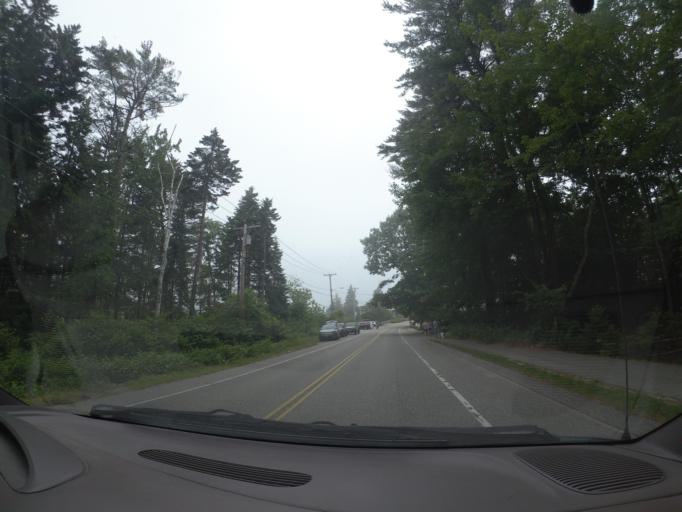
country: US
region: Maine
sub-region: York County
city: Kennebunkport
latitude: 43.3513
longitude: -70.4793
